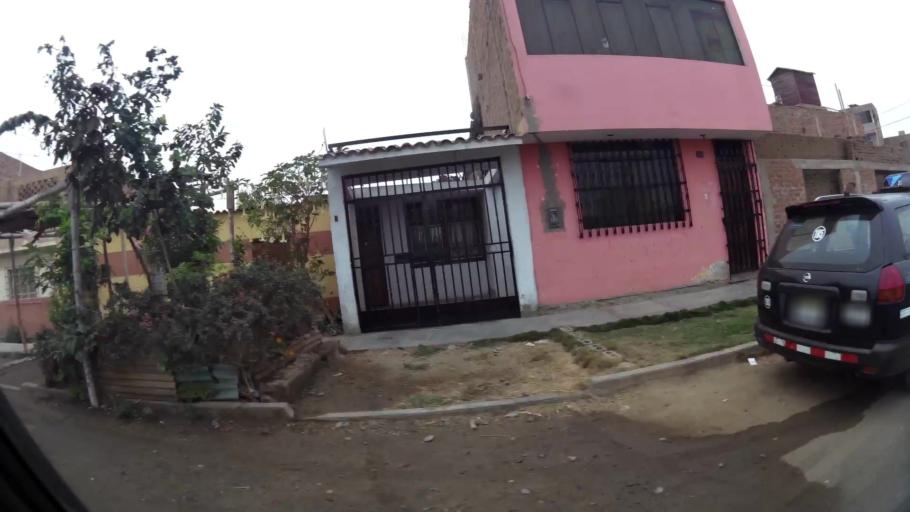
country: PE
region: La Libertad
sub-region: Provincia de Trujillo
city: La Esperanza
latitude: -8.0815
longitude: -79.0527
